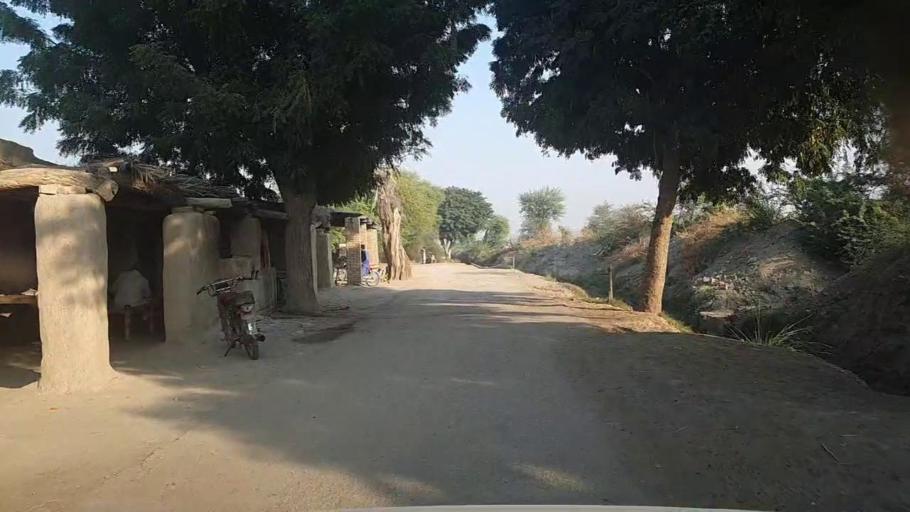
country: PK
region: Sindh
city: Kandiari
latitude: 26.7202
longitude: 68.4957
